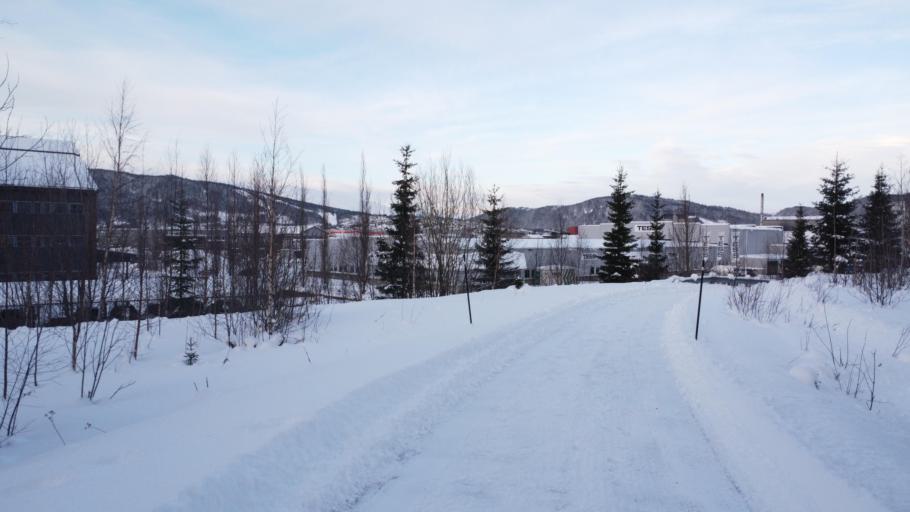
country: NO
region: Nordland
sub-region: Rana
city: Mo i Rana
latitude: 66.3200
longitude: 14.1545
